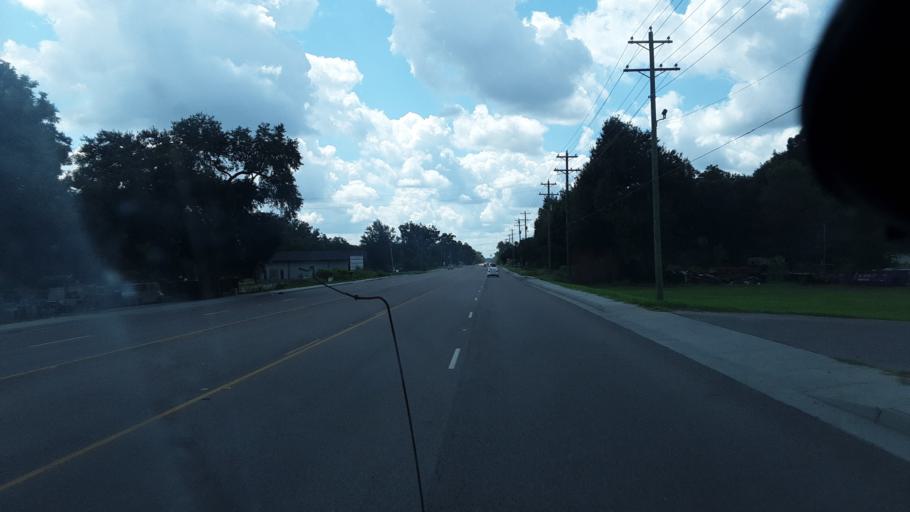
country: US
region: South Carolina
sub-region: Berkeley County
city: Moncks Corner
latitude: 33.1564
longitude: -80.0588
